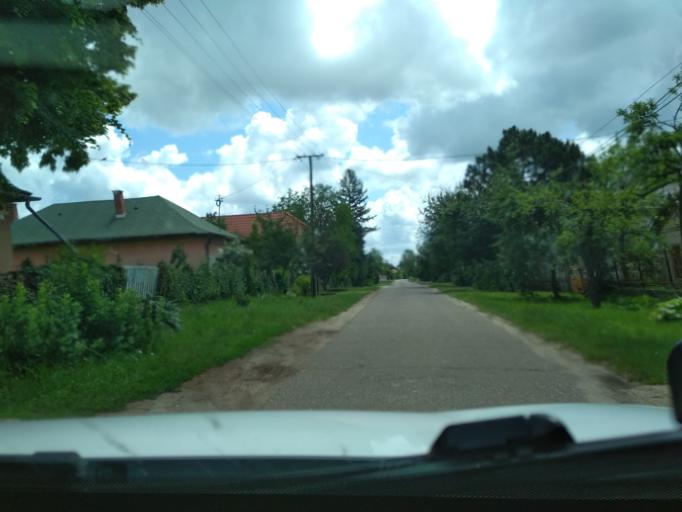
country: HU
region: Jasz-Nagykun-Szolnok
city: Tiszafured
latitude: 47.6069
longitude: 20.7551
